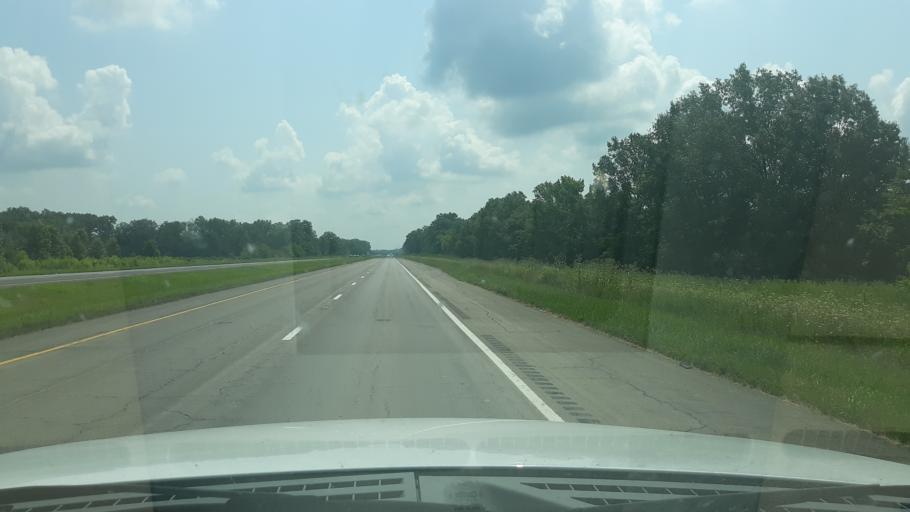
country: US
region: Illinois
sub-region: Saline County
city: Carrier Mills
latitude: 37.7334
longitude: -88.6466
